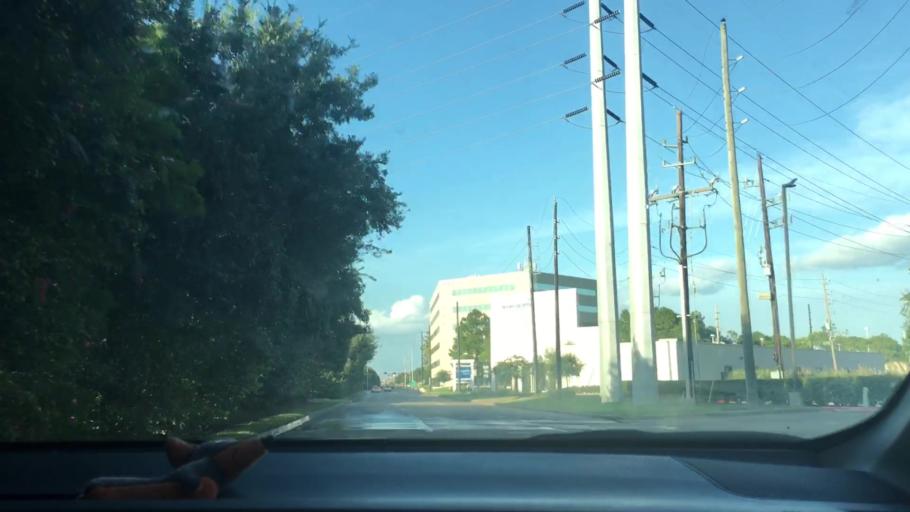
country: US
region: Texas
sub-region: Fort Bend County
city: Meadows Place
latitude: 29.6366
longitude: -95.5836
